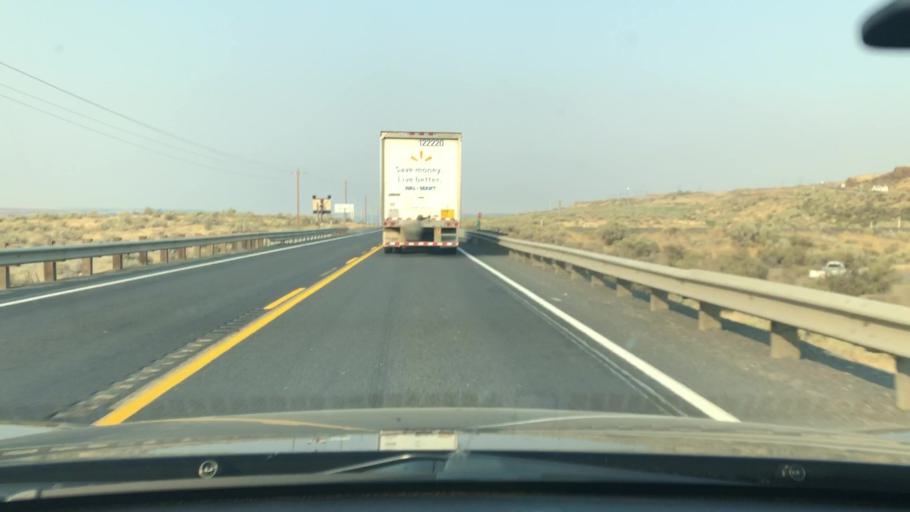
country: US
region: Oregon
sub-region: Umatilla County
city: Stanfield
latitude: 45.9151
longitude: -119.1354
